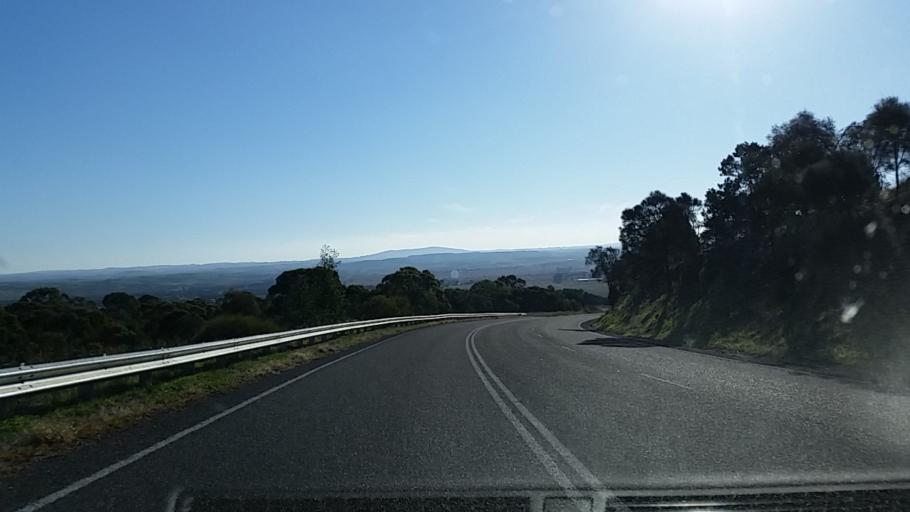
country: AU
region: South Australia
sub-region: Mount Barker
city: Callington
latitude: -35.1144
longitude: 139.0672
